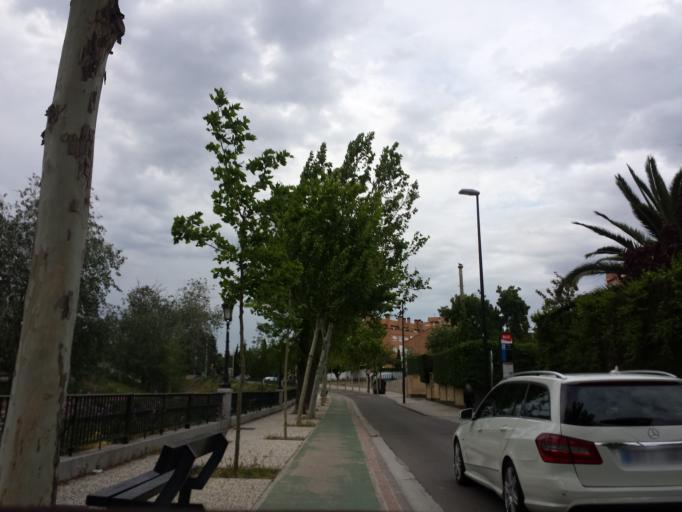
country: ES
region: Aragon
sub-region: Provincia de Zaragoza
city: Delicias
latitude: 41.6268
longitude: -0.9073
